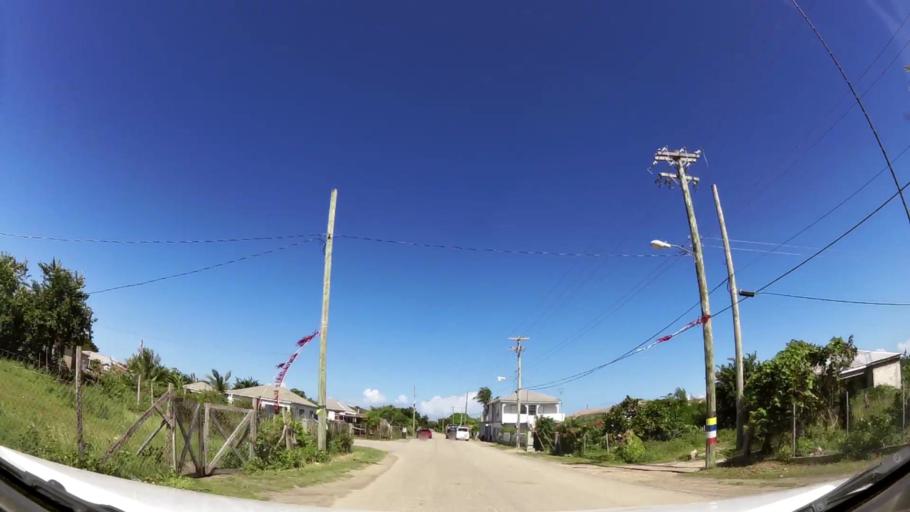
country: AG
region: Barbuda
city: Codrington
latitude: 17.6382
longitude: -61.8232
